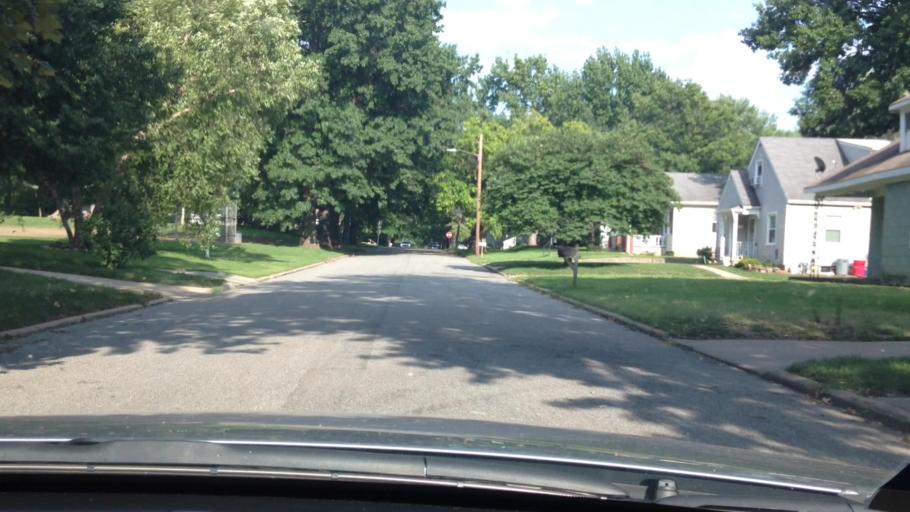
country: US
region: Kansas
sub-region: Leavenworth County
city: Leavenworth
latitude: 39.3232
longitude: -94.9322
